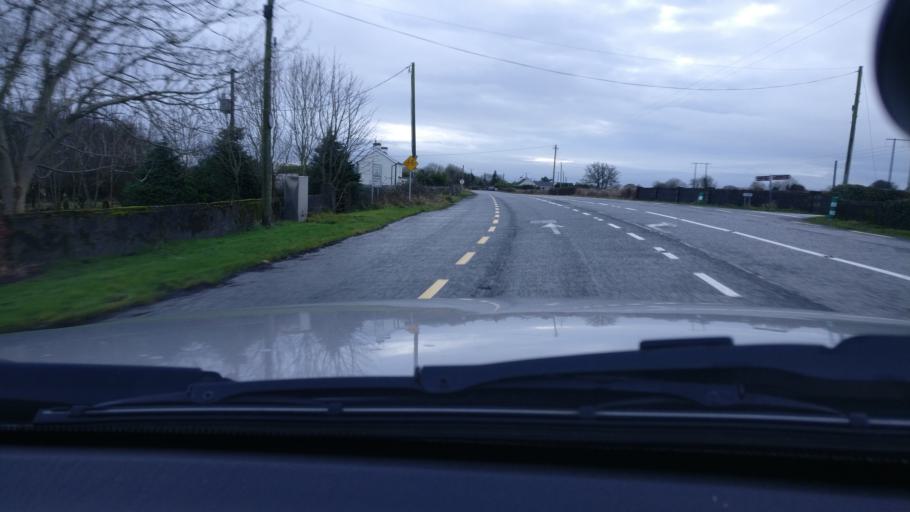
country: IE
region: Leinster
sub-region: An Iarmhi
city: Athlone
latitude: 53.3913
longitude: -7.9916
